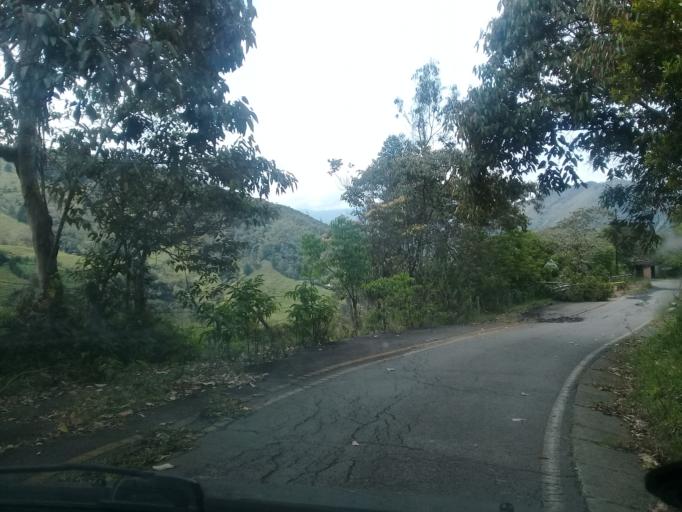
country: CO
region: Cundinamarca
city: Gachala
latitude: 4.6999
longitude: -73.4550
